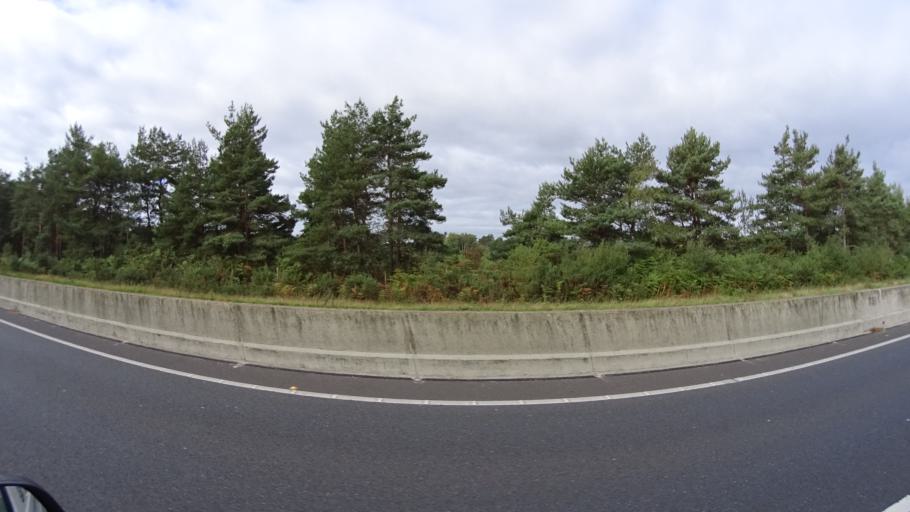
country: GB
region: England
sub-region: Dorset
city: Christchurch
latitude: 50.7789
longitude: -1.8098
